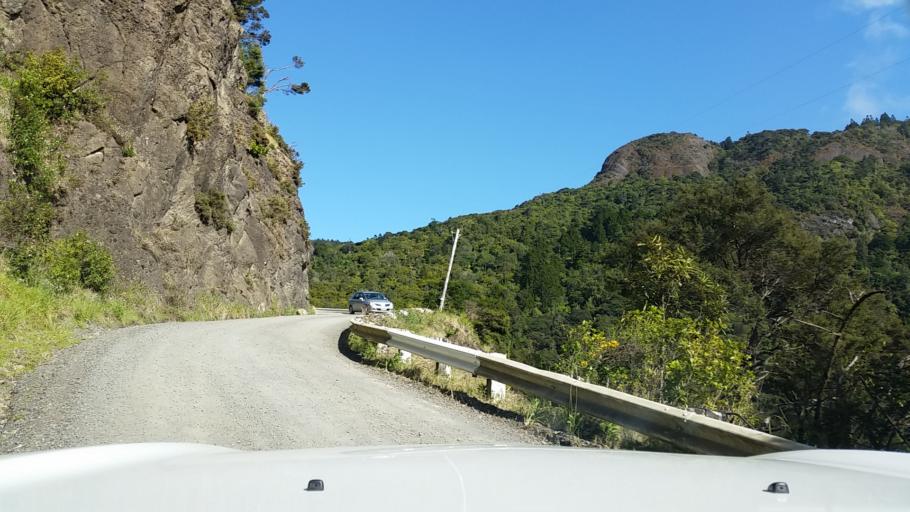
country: NZ
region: Auckland
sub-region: Auckland
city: Titirangi
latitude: -37.0205
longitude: 174.5442
